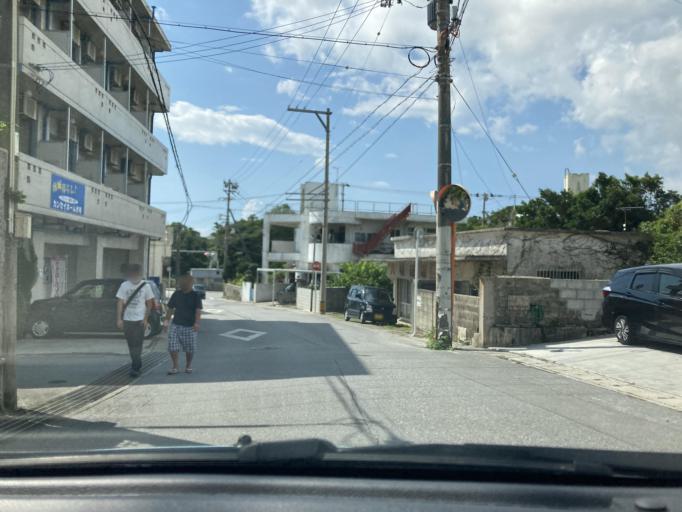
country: JP
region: Okinawa
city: Tomigusuku
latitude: 26.1435
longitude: 127.7681
